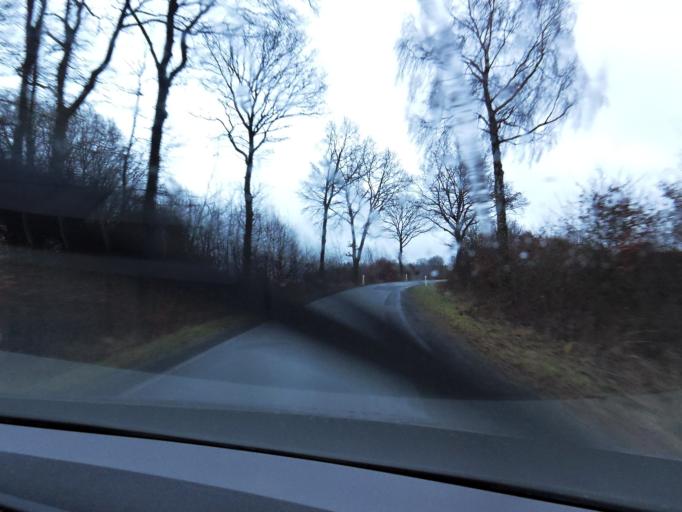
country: DE
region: Schleswig-Holstein
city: Mustin
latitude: 53.6610
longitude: 10.8678
